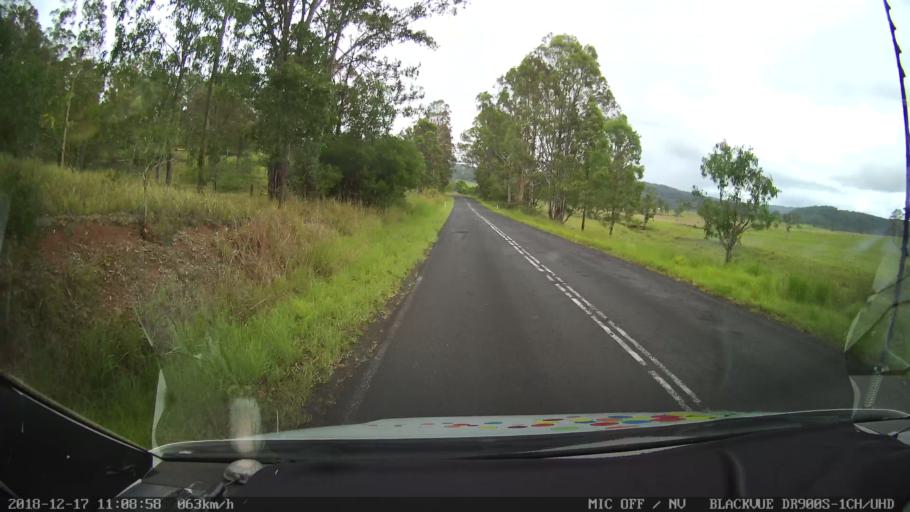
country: AU
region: New South Wales
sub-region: Kyogle
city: Kyogle
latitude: -28.7586
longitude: 152.6555
